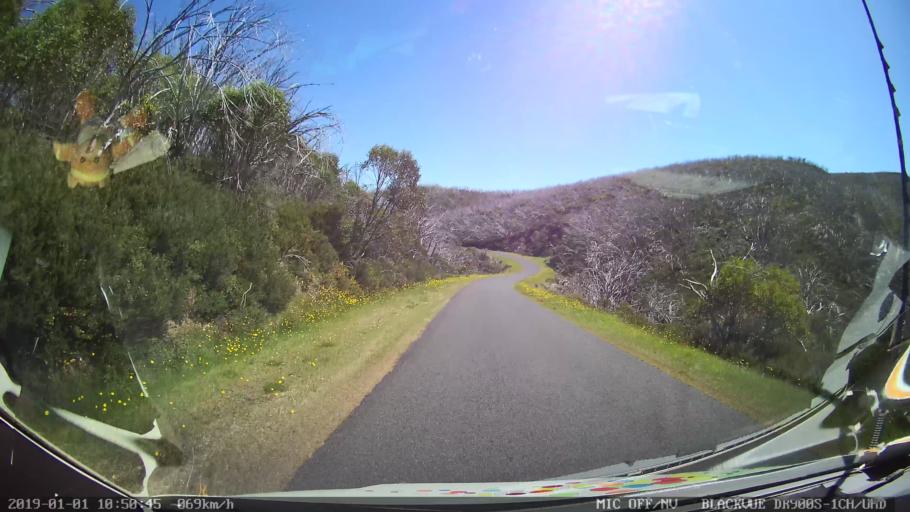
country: AU
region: New South Wales
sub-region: Snowy River
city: Jindabyne
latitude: -36.0255
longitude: 148.3716
